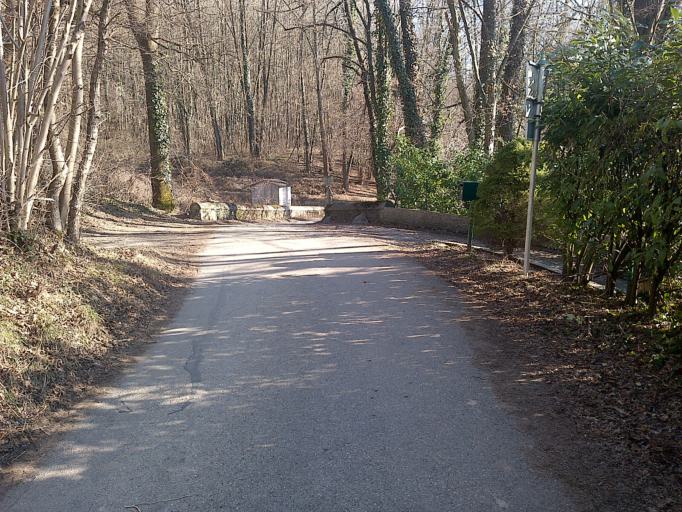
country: FR
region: Rhone-Alpes
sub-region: Departement de l'Isere
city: Poisat
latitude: 45.1445
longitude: 5.7702
